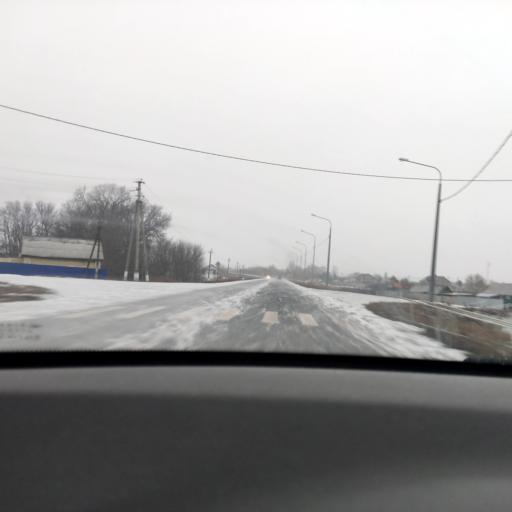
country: RU
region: Samara
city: Krasnoarmeyskoye
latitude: 52.8968
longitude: 49.9655
